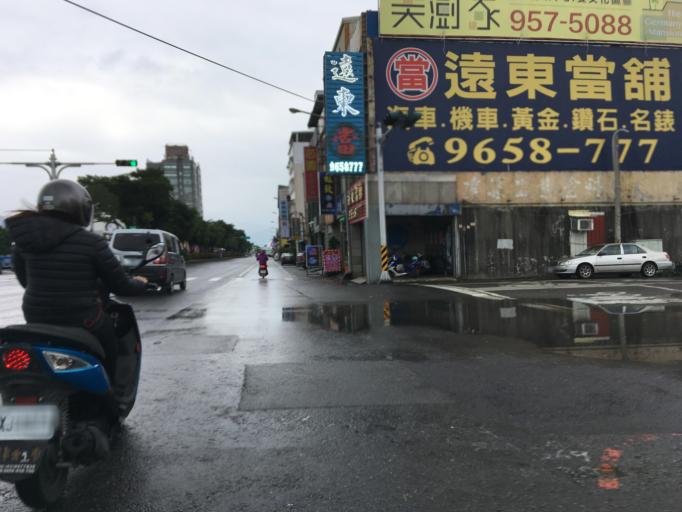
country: TW
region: Taiwan
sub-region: Yilan
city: Yilan
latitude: 24.7095
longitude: 121.7723
